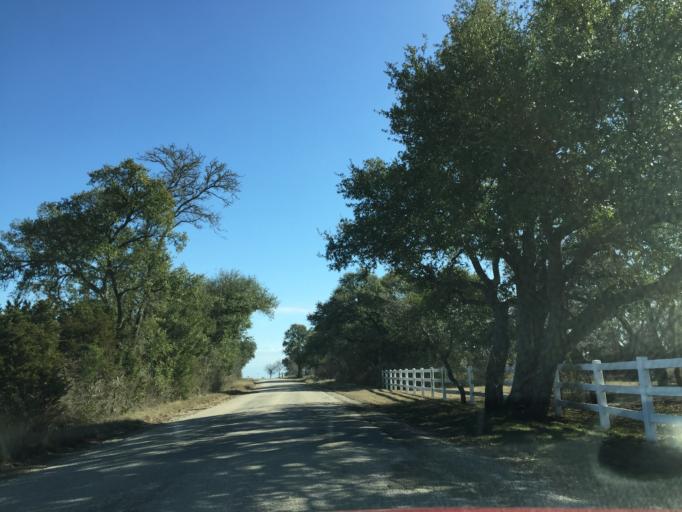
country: US
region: Texas
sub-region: Williamson County
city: Florence
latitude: 30.7736
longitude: -97.8899
